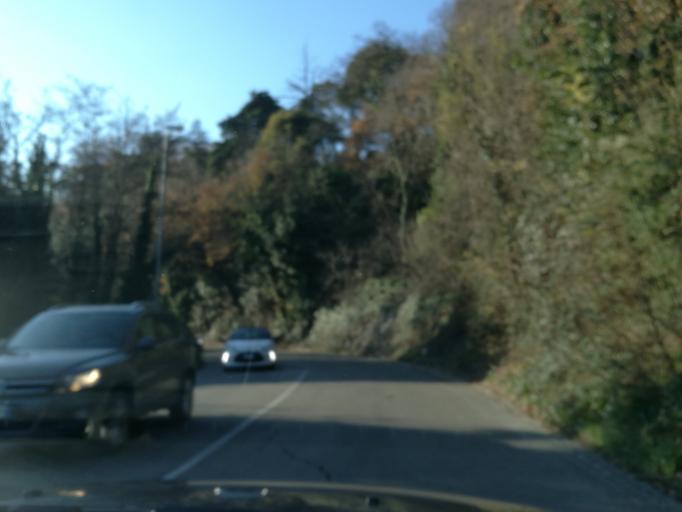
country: IT
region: Umbria
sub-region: Provincia di Perugia
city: Perugia
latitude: 43.0927
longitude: 12.4005
